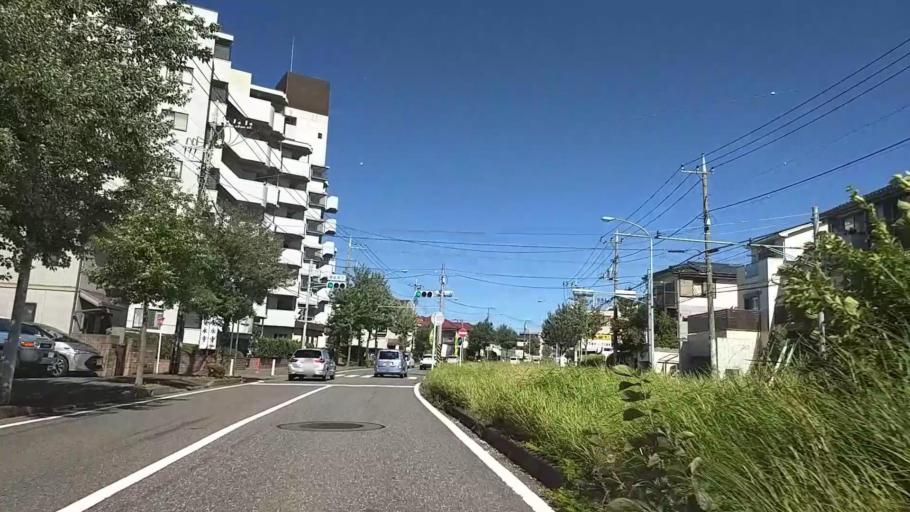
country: JP
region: Tokyo
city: Chofugaoka
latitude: 35.5829
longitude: 139.5444
